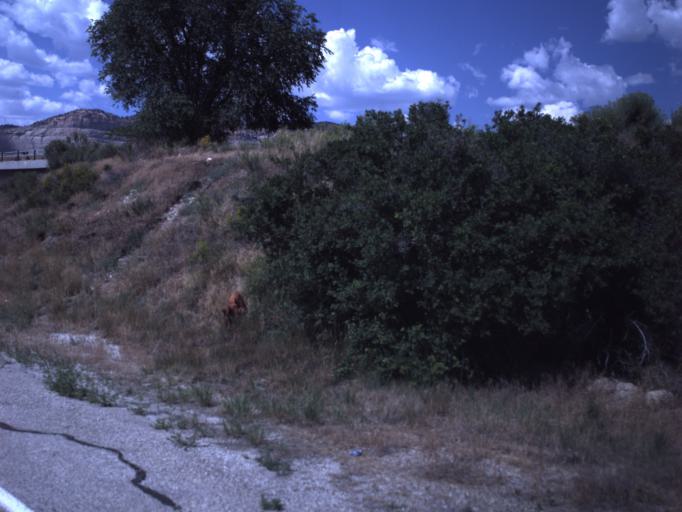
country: US
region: Utah
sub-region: Carbon County
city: Spring Glen
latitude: 39.6653
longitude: -110.8558
